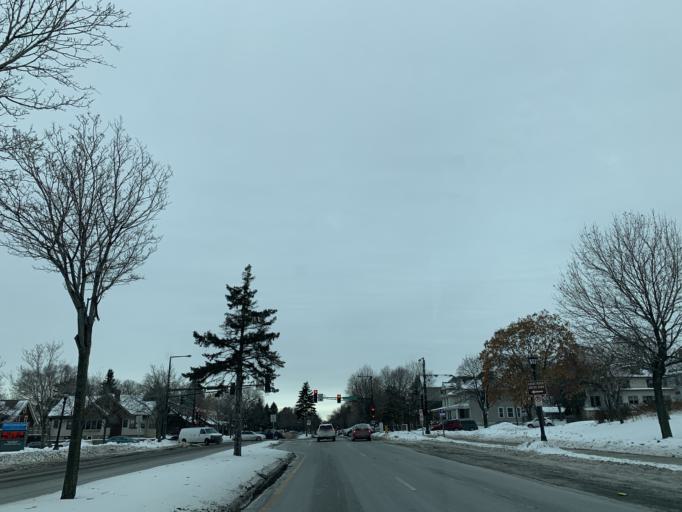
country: US
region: Minnesota
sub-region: Ramsey County
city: Falcon Heights
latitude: 44.9494
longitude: -93.1467
